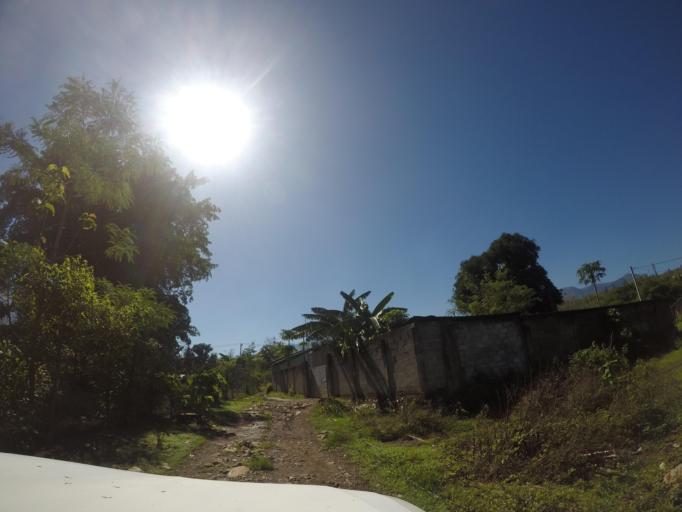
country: TL
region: Bobonaro
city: Maliana
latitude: -8.9911
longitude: 125.2165
